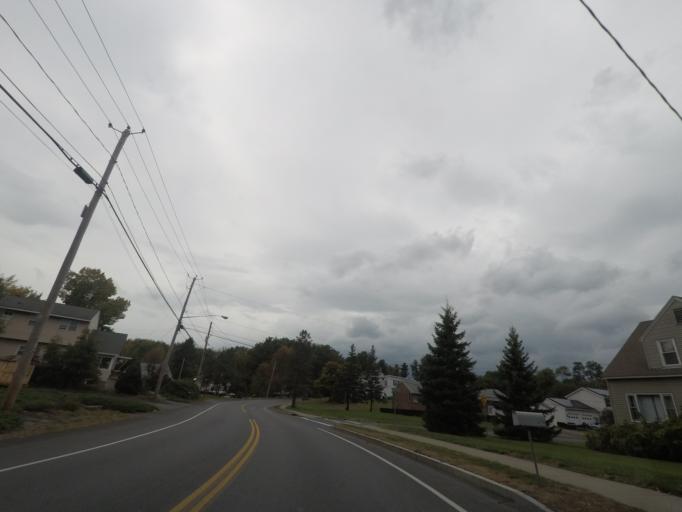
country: US
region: New York
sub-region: Albany County
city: McKownville
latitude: 42.6713
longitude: -73.8462
